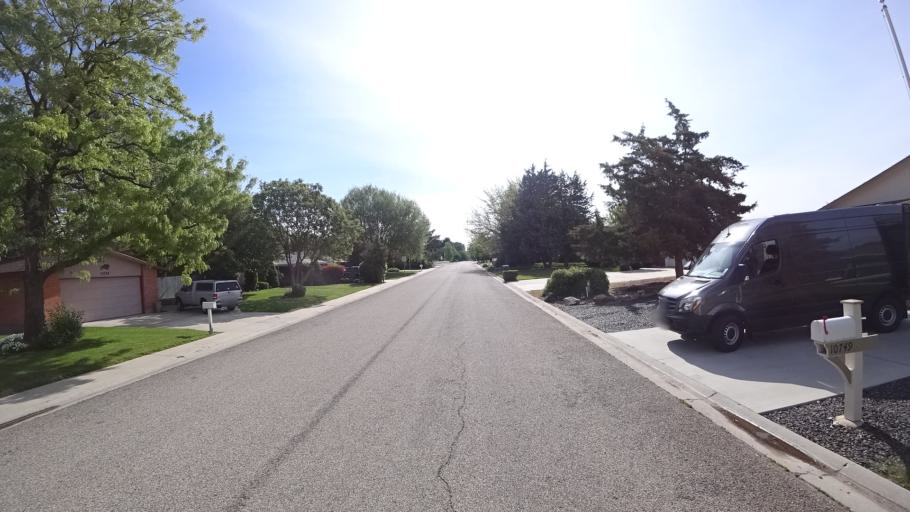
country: US
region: Idaho
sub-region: Ada County
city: Meridian
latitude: 43.5657
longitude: -116.3160
